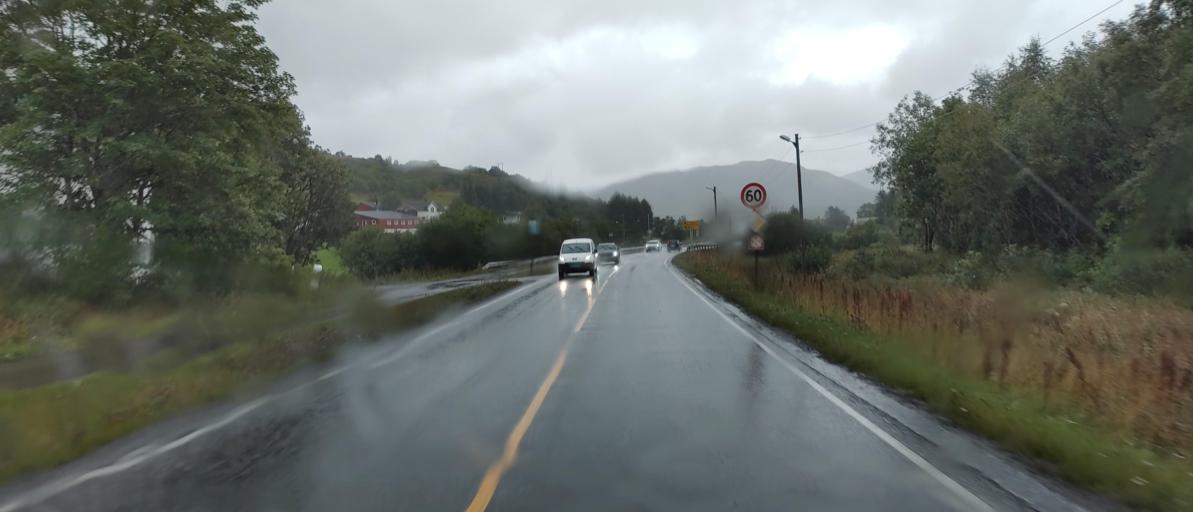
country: NO
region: Nordland
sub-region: Vestvagoy
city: Evjen
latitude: 68.2513
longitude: 13.7648
